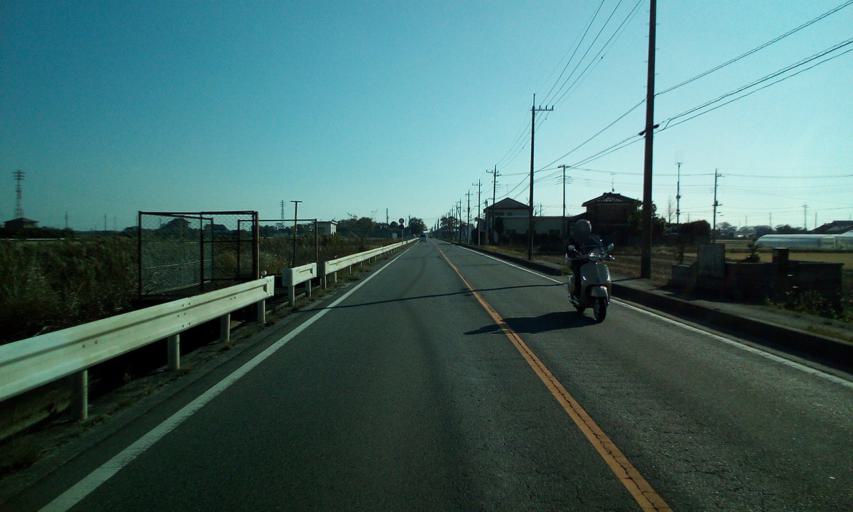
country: JP
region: Saitama
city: Sugito
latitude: 36.0273
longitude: 139.7885
